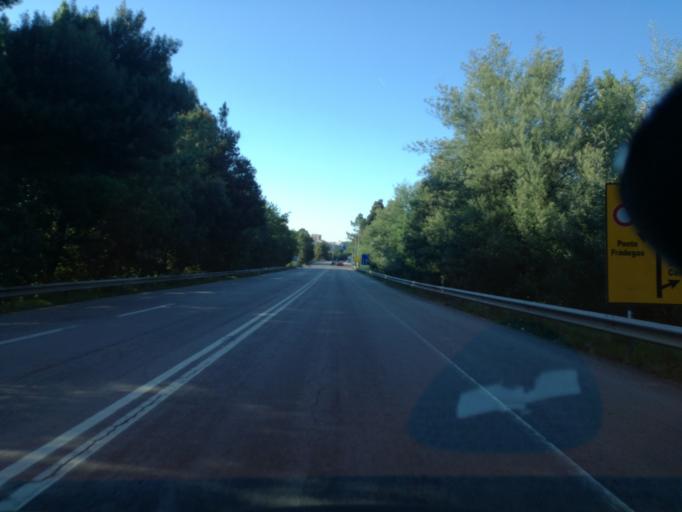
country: PT
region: Porto
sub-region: Santo Tirso
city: Sao Miguel do Couto
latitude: 41.3247
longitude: -8.4694
